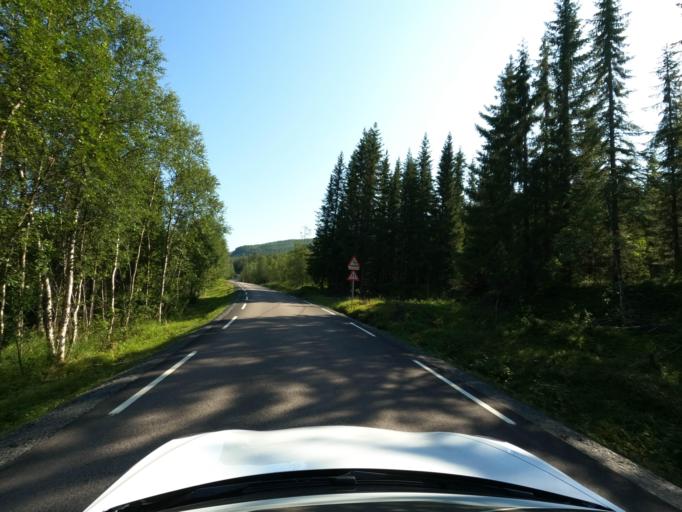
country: NO
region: Nordland
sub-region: Narvik
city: Narvik
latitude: 68.3882
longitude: 17.3411
